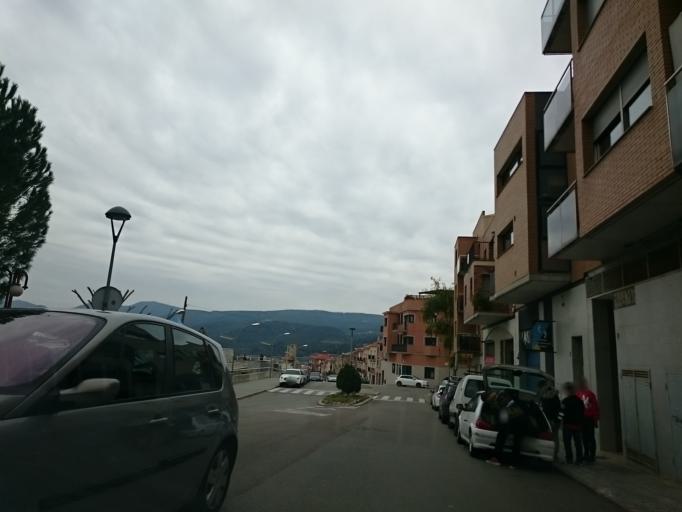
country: ES
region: Catalonia
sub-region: Provincia de Barcelona
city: Sant Sadurni d'Anoia
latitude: 41.4286
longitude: 1.7855
